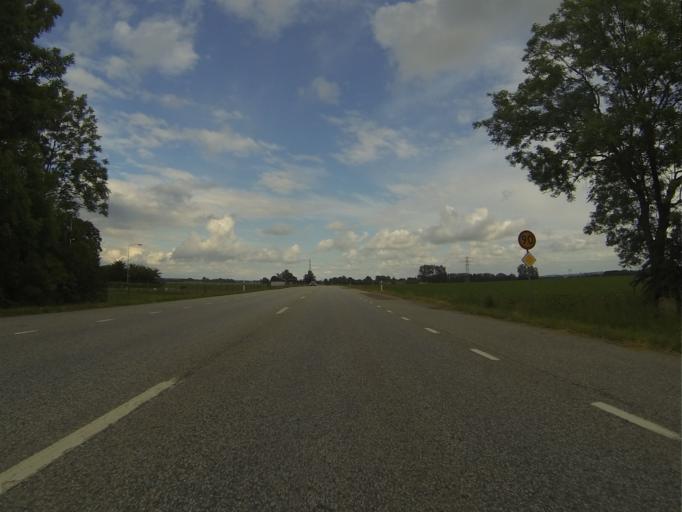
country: SE
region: Skane
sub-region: Staffanstorps Kommun
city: Hjaerup
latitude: 55.6426
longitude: 13.1367
